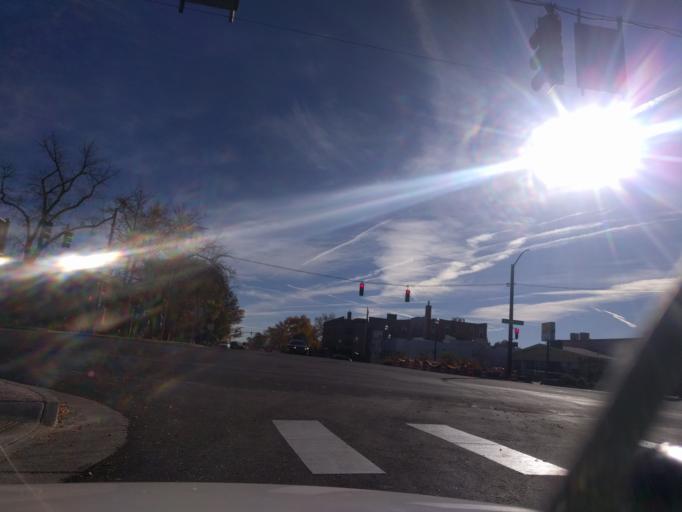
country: US
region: Colorado
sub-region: El Paso County
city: Colorado Springs
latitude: 38.8383
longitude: -104.8255
